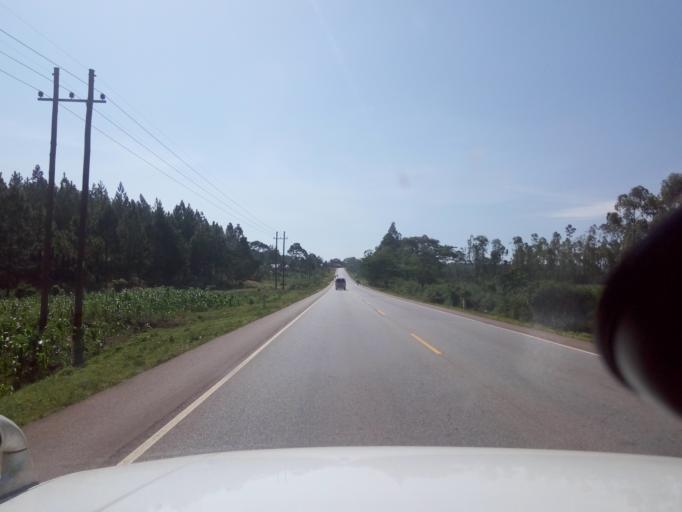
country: UG
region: Eastern Region
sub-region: Busia District
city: Busia
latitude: 0.5302
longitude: 33.9380
